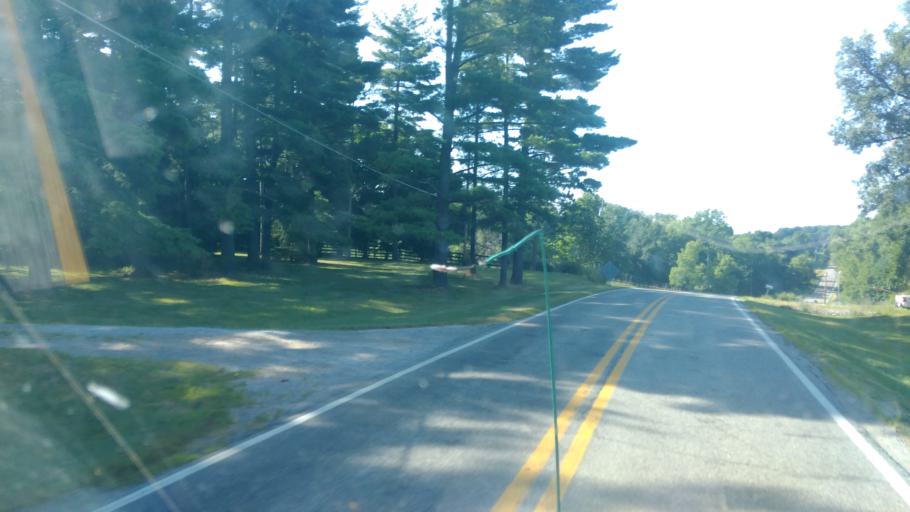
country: US
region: Ohio
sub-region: Delaware County
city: Delaware
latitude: 40.3400
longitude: -83.0518
